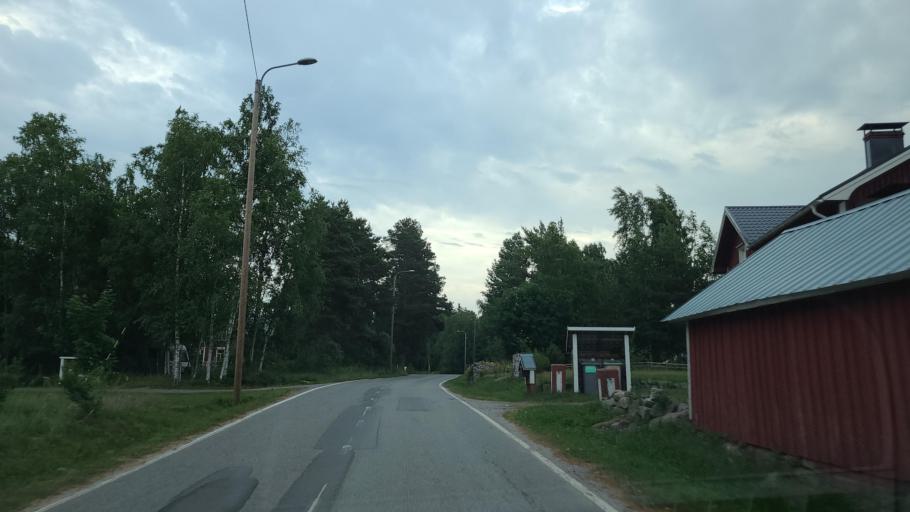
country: FI
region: Ostrobothnia
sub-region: Vaasa
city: Replot
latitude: 63.1676
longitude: 21.2595
